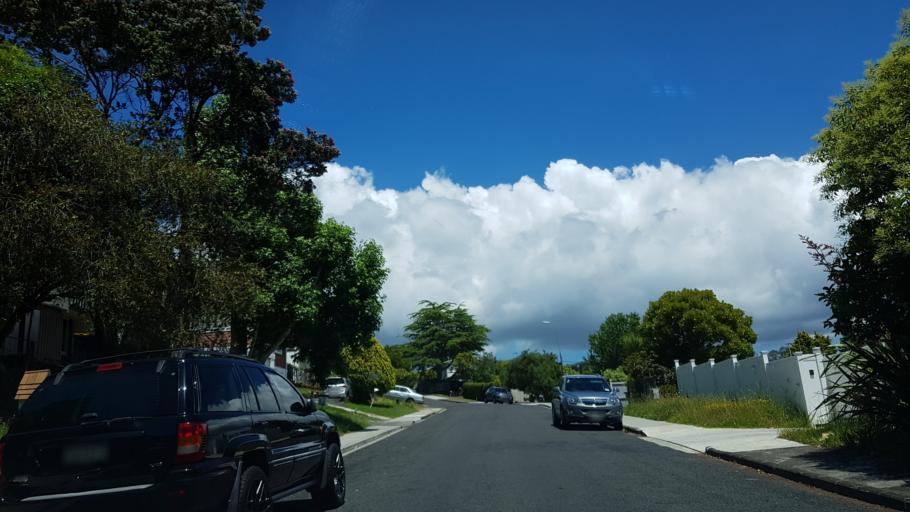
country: NZ
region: Auckland
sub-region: Auckland
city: North Shore
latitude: -36.7985
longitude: 174.7036
